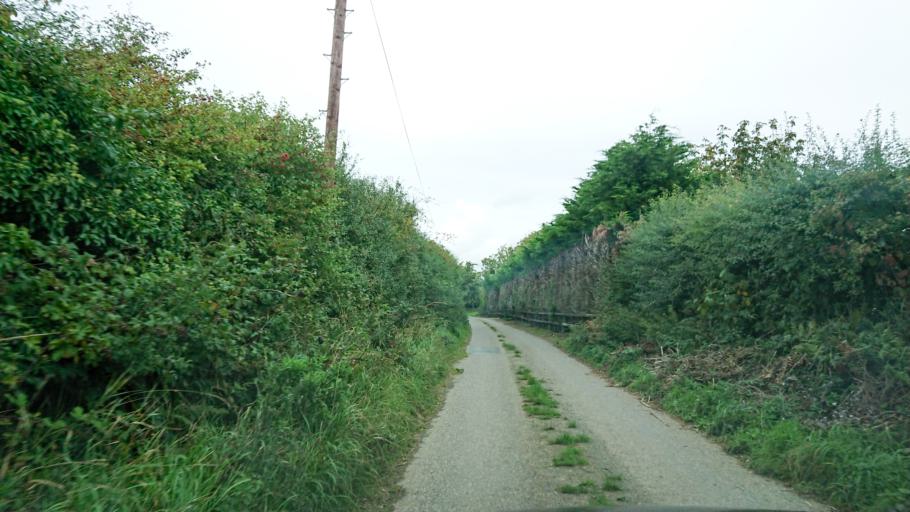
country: IE
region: Munster
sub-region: Waterford
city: Dunmore East
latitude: 52.2087
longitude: -7.0431
